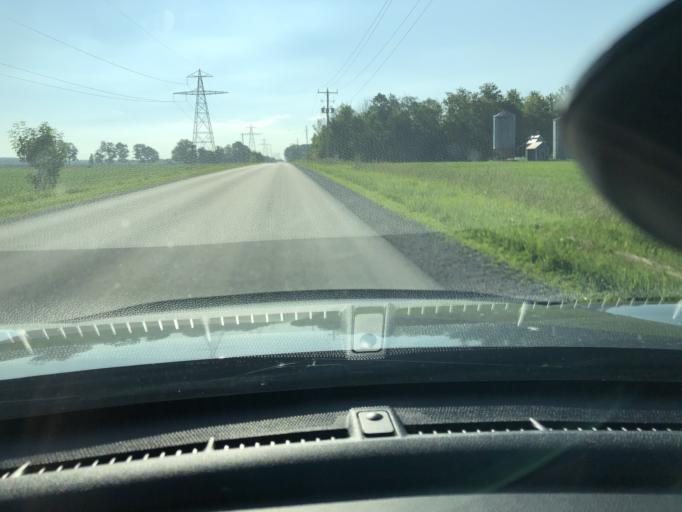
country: CA
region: Ontario
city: Stratford
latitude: 43.3880
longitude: -80.8544
